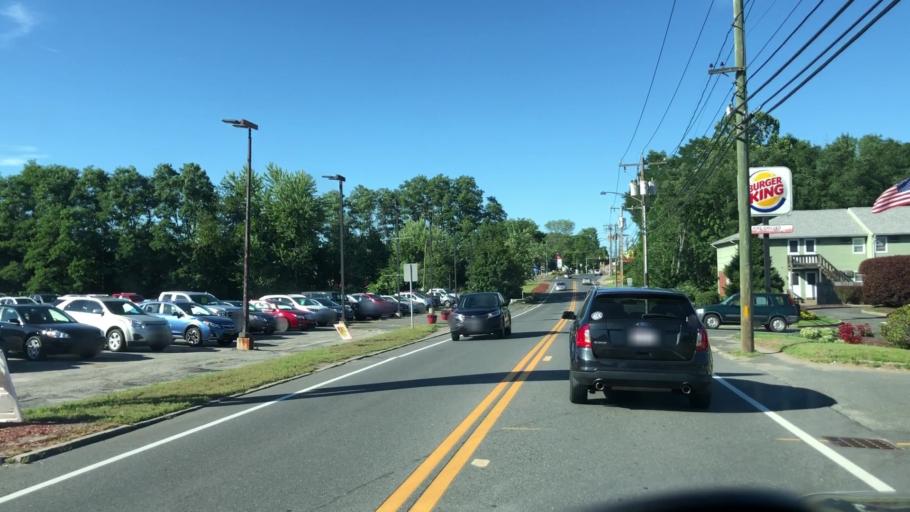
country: US
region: Massachusetts
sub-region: Hampshire County
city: Easthampton
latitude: 42.2786
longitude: -72.6718
